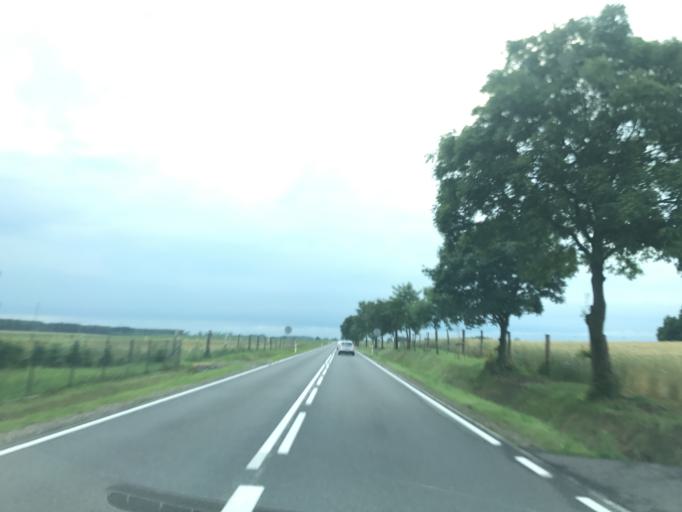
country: PL
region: Pomeranian Voivodeship
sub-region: Powiat czluchowski
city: Rzeczenica
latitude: 53.7519
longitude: 17.1429
